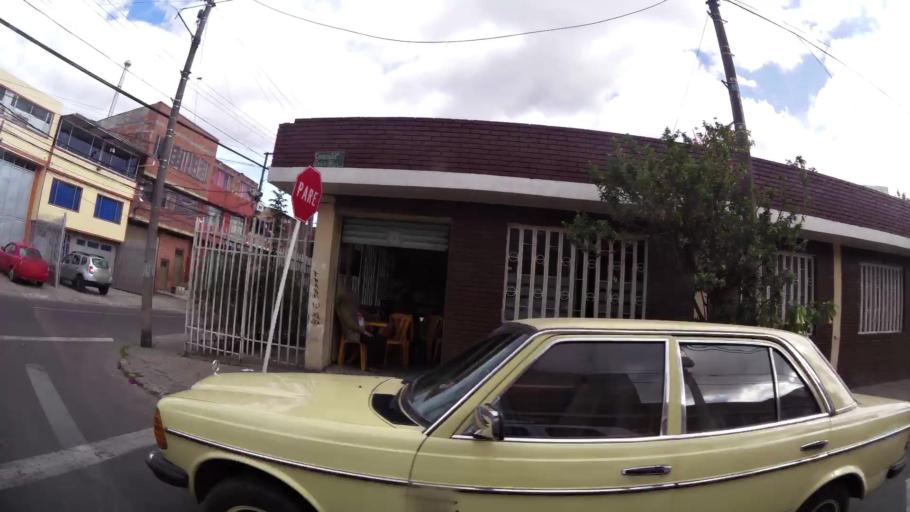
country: CO
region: Bogota D.C.
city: Bogota
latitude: 4.6102
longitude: -74.1371
